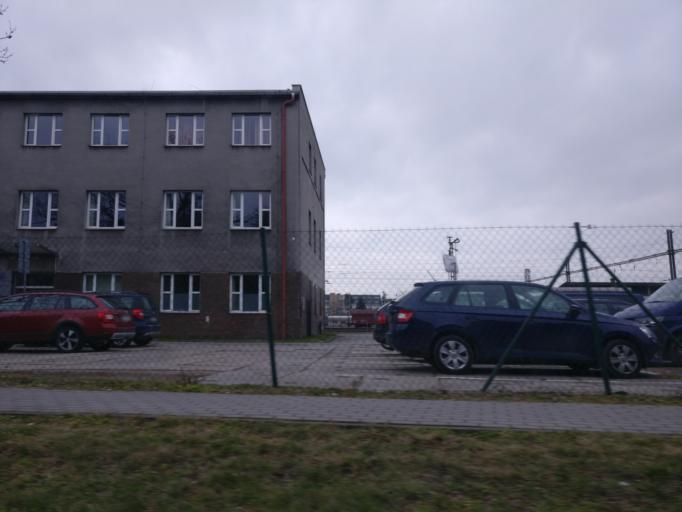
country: CZ
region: Pardubicky
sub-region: Okres Pardubice
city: Pardubice
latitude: 50.0323
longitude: 15.7642
